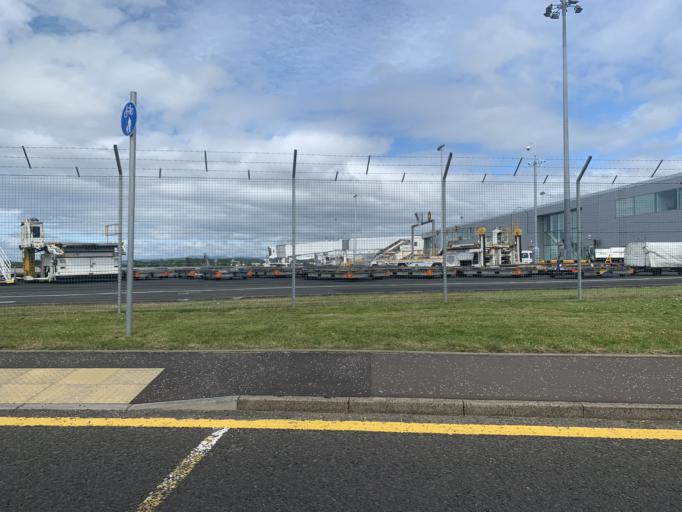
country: GB
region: Scotland
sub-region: Renfrewshire
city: Inchinnan
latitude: 55.8637
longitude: -4.4369
